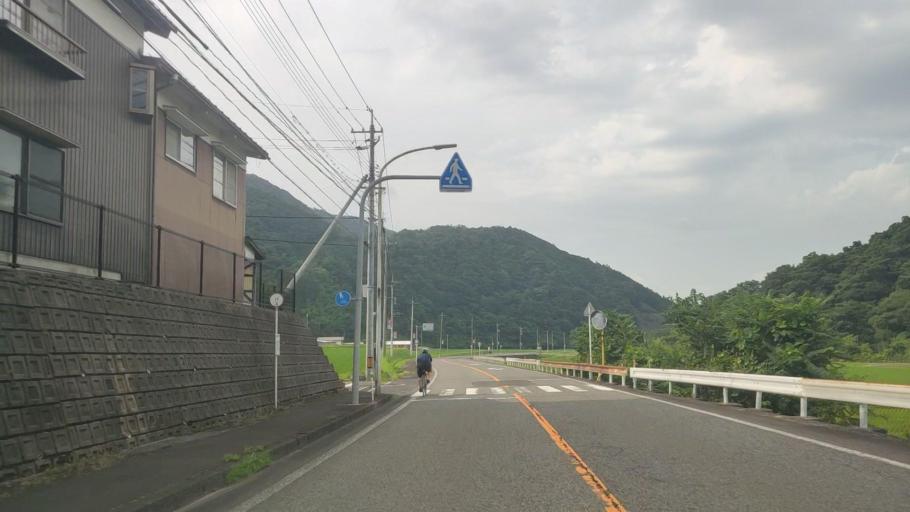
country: JP
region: Tottori
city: Kurayoshi
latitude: 35.3581
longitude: 133.8461
